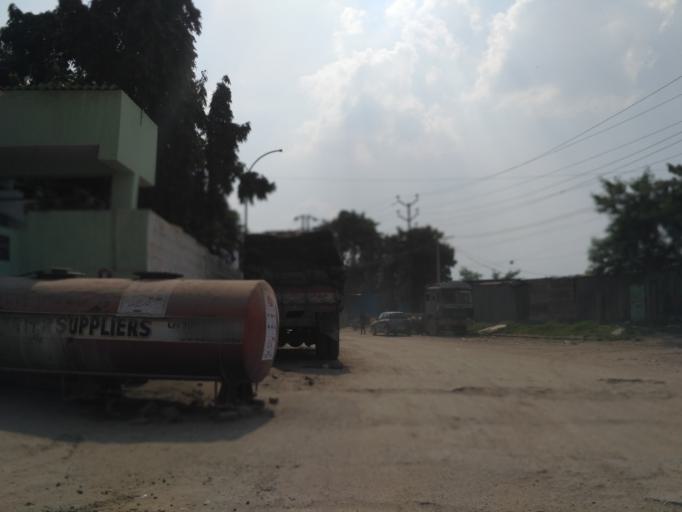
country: IN
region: Telangana
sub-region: Rangareddi
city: Kukatpalli
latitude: 17.4639
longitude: 78.4194
